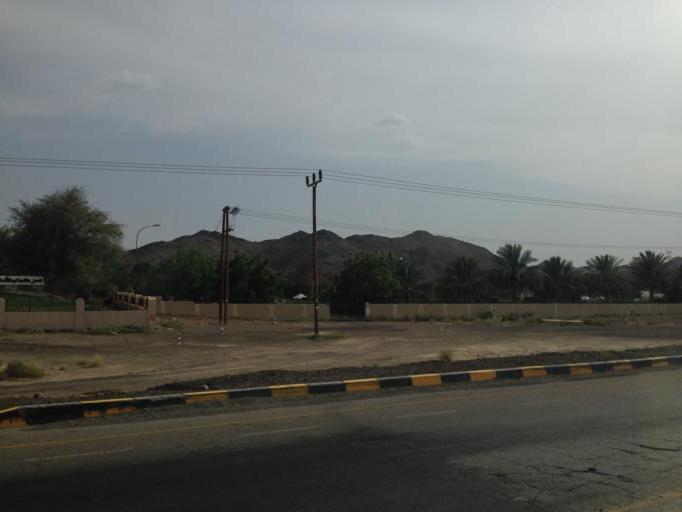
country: OM
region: Ash Sharqiyah
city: Al Qabil
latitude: 22.6454
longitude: 58.6260
